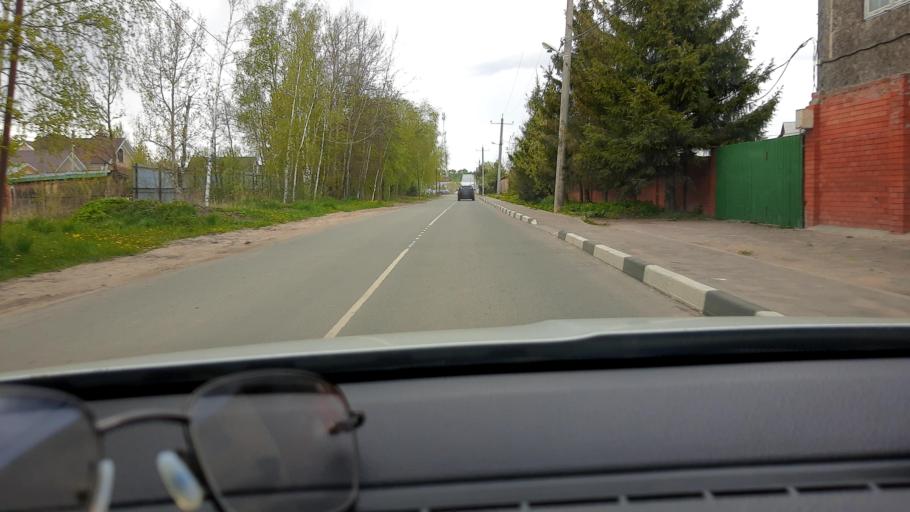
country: RU
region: Moskovskaya
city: Skhodnya
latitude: 55.8909
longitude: 37.3053
